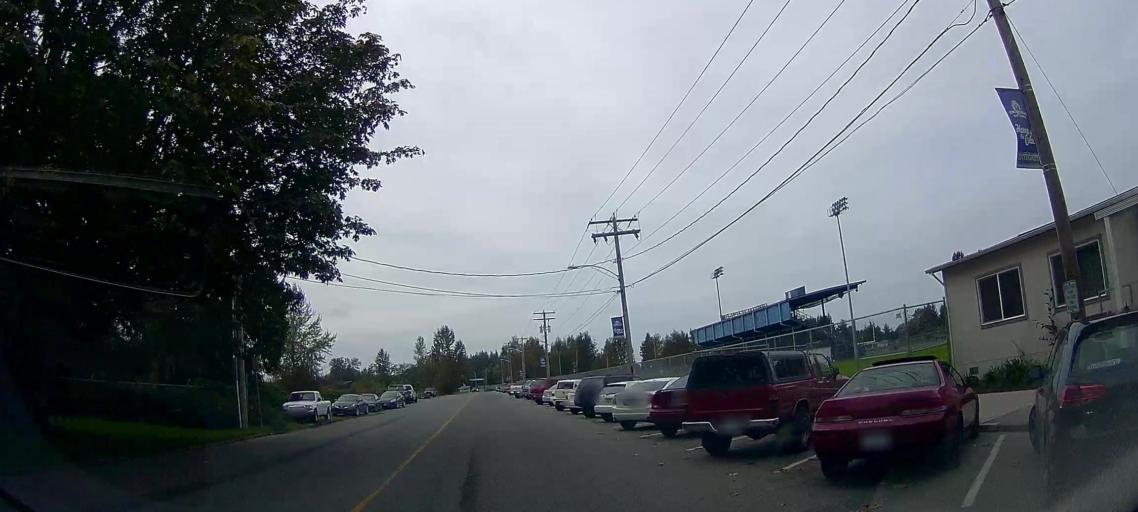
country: US
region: Washington
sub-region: Skagit County
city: Sedro-Woolley
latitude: 48.4989
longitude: -122.2384
